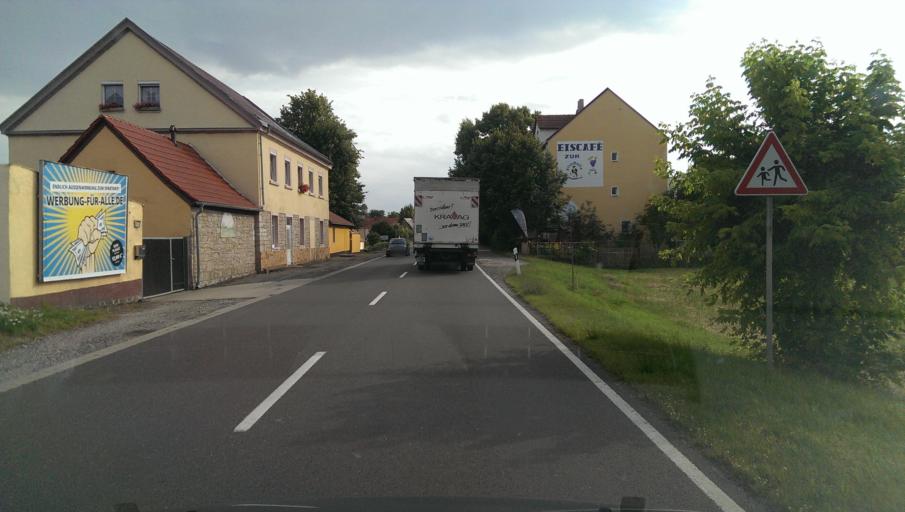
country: DE
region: Saxony
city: Elstertrebnitz
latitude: 51.1309
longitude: 12.2190
